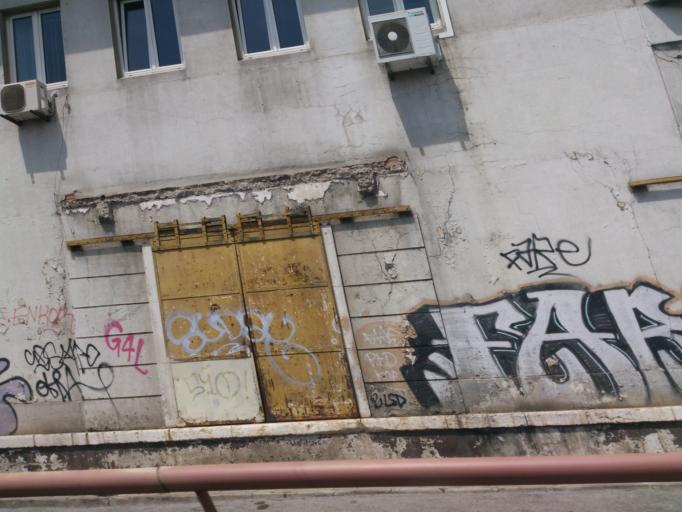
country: PT
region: Lisbon
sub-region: Lisbon
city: Lisbon
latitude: 38.7175
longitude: -9.1184
